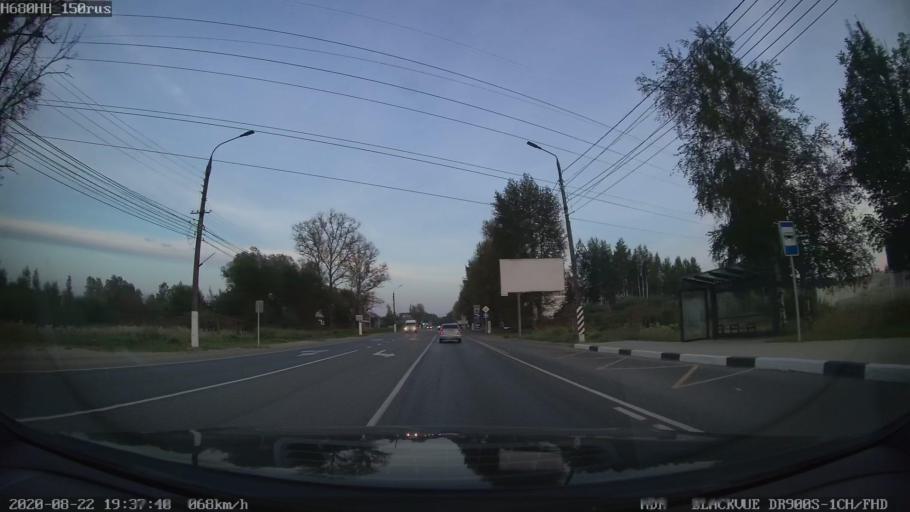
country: RU
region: Tverskaya
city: Tver
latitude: 56.8169
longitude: 35.9863
